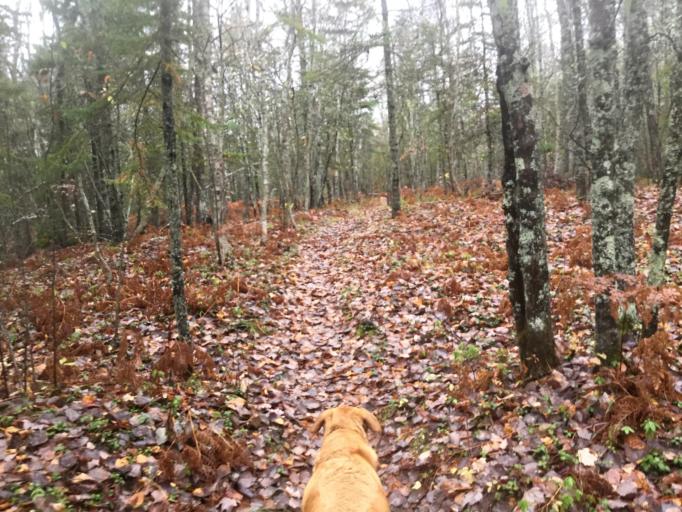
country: CA
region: Nova Scotia
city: New Glasgow
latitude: 45.5540
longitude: -62.6793
